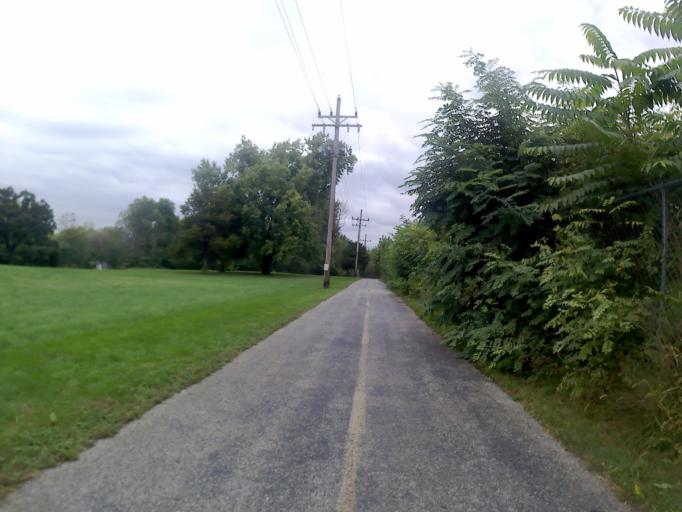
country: US
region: Illinois
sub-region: Kendall County
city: Oswego
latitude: 41.6939
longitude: -88.3478
